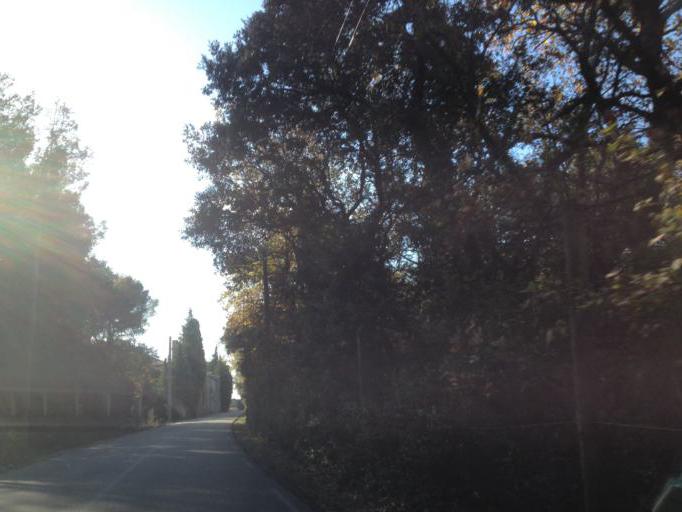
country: FR
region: Provence-Alpes-Cote d'Azur
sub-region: Departement du Vaucluse
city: Jonquieres
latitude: 44.1163
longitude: 4.8763
